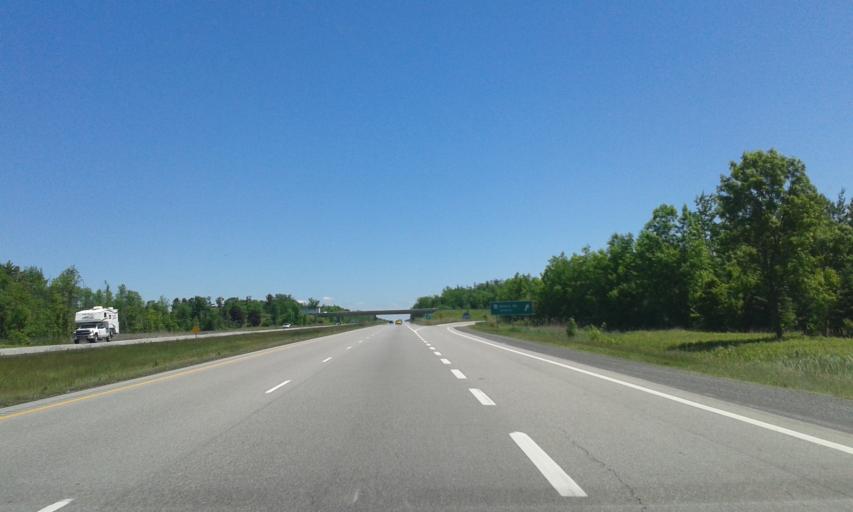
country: US
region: New York
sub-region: St. Lawrence County
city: Ogdensburg
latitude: 44.8074
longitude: -75.4101
